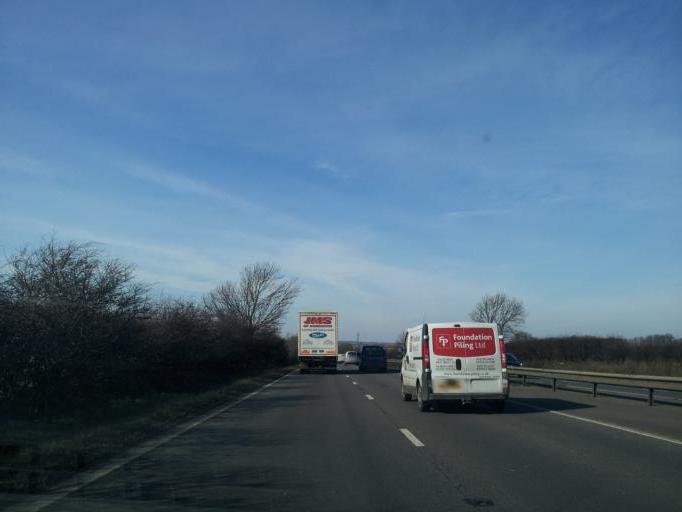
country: GB
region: England
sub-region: Lincolnshire
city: Stamford
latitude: 52.6333
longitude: -0.4756
